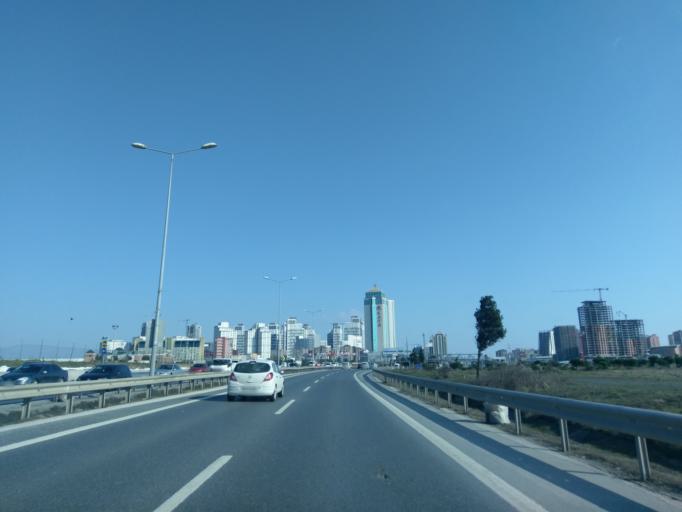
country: TR
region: Istanbul
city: Gurpinar
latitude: 41.0256
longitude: 28.6190
